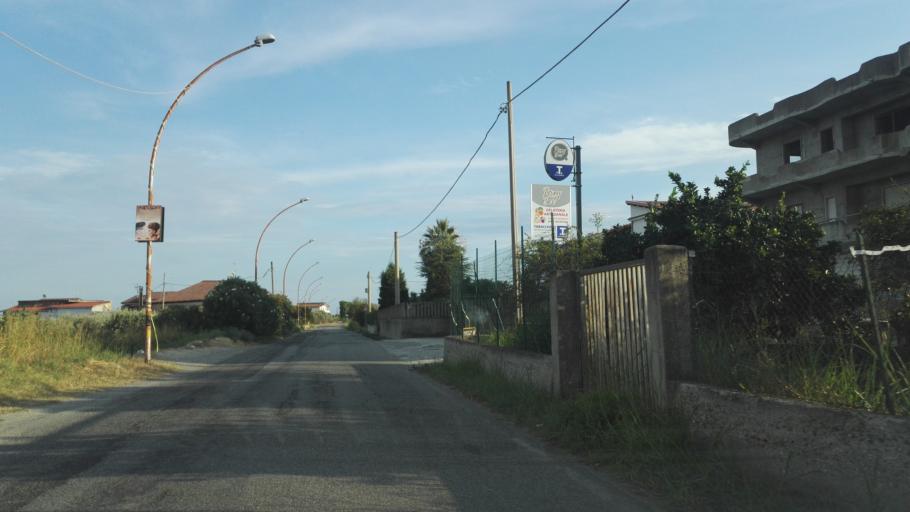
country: IT
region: Calabria
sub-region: Provincia di Reggio Calabria
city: Caulonia Marina
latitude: 38.3644
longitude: 16.4846
